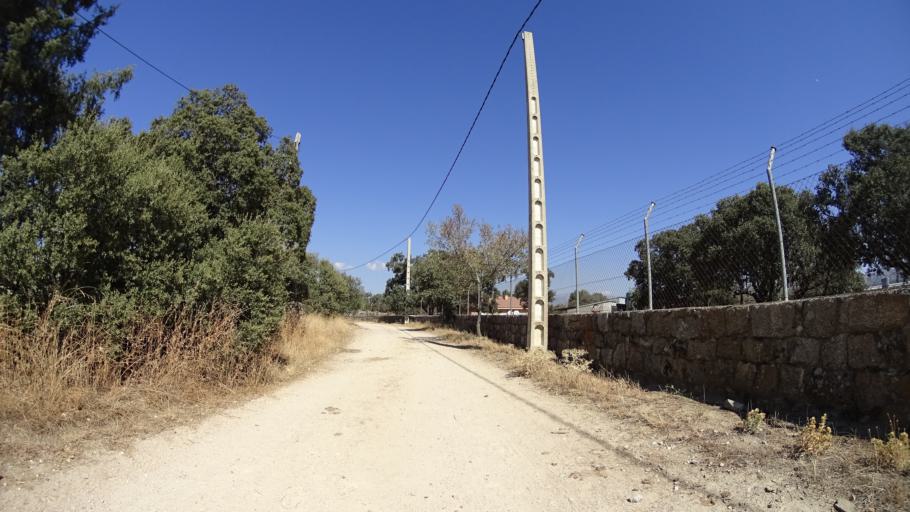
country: ES
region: Madrid
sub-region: Provincia de Madrid
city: Collado-Villalba
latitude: 40.6128
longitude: -4.0037
